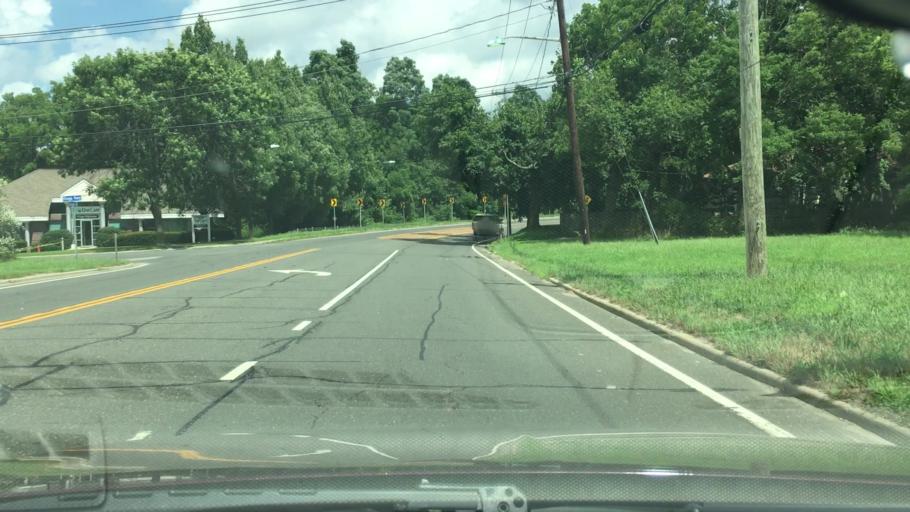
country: US
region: New York
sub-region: Suffolk County
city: Hauppauge
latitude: 40.8150
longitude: -73.2182
